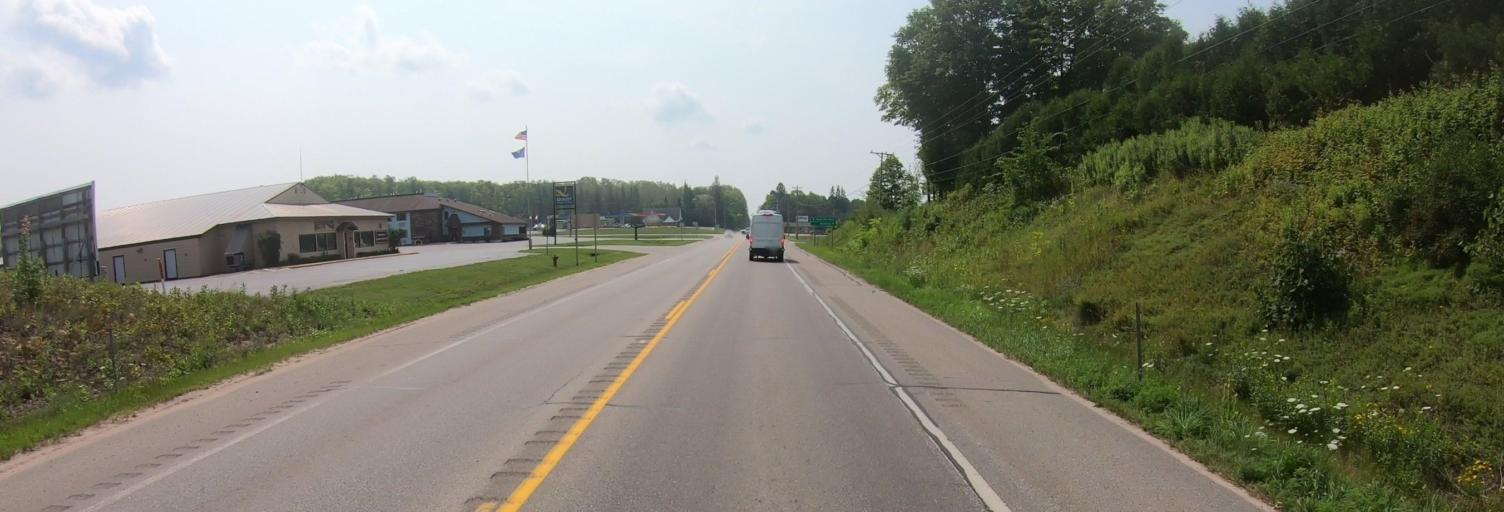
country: US
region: Michigan
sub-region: Luce County
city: Newberry
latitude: 46.3054
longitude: -85.5095
